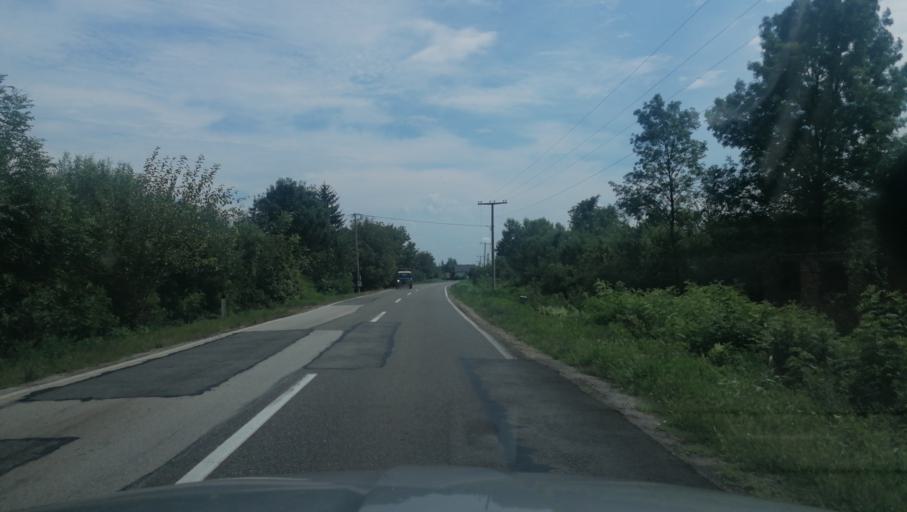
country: BA
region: Republika Srpska
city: Bosanski Samac
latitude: 45.0373
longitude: 18.5110
